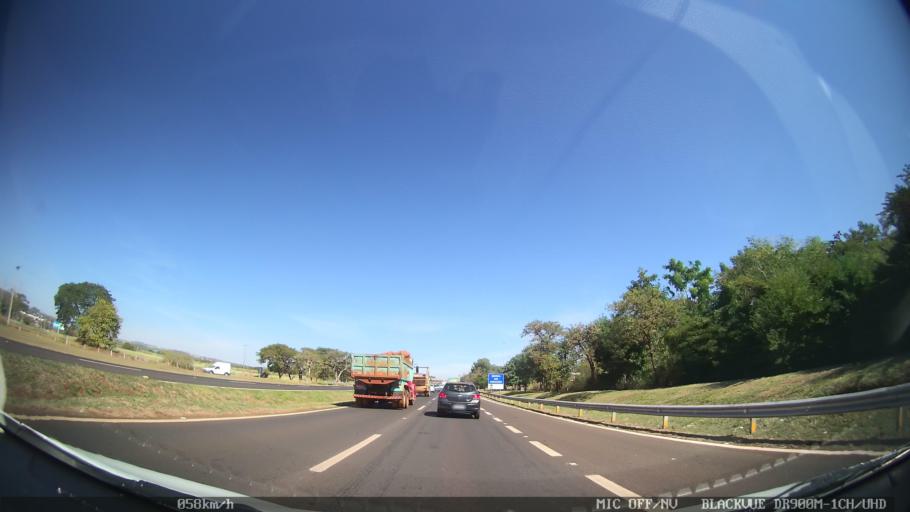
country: BR
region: Sao Paulo
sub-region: Ribeirao Preto
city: Ribeirao Preto
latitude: -21.2165
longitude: -47.7740
